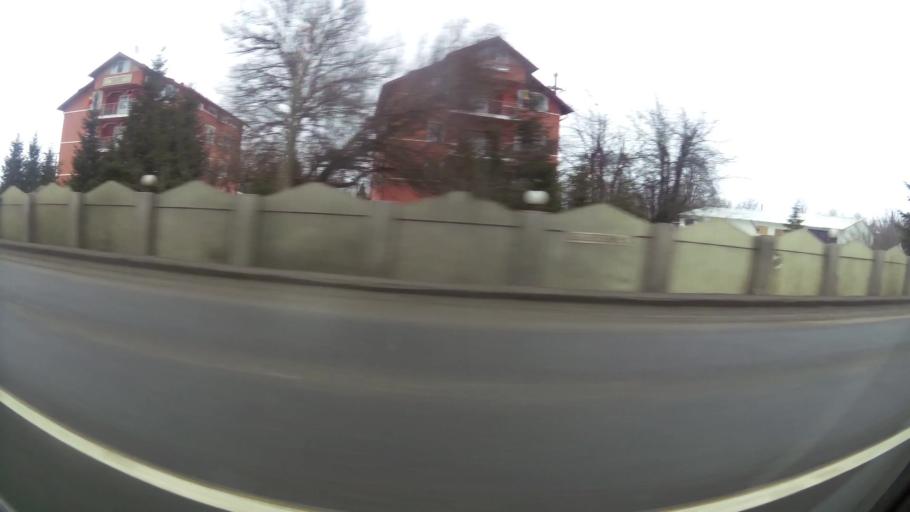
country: RO
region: Ilfov
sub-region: Comuna Bragadiru
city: Bragadiru
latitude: 44.3919
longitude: 25.9843
